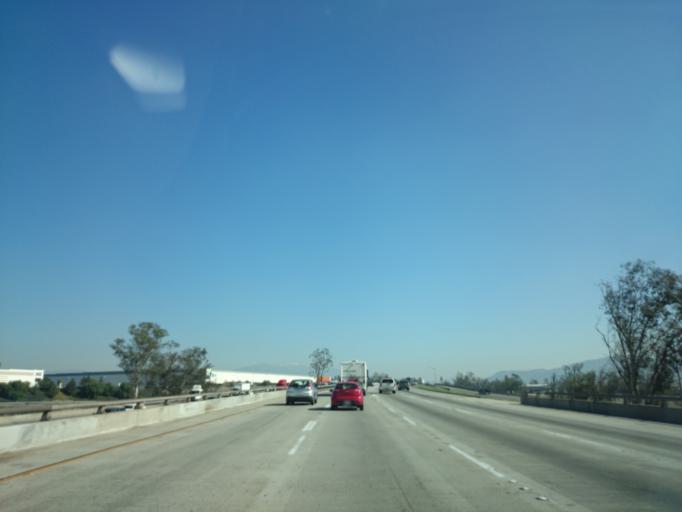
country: US
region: California
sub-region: Riverside County
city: Glen Avon
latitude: 34.0676
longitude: -117.5176
